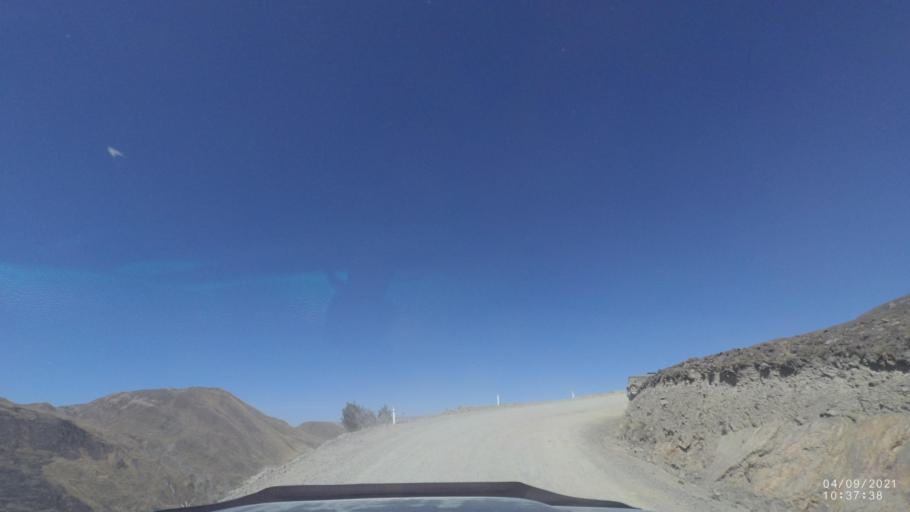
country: BO
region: Cochabamba
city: Sipe Sipe
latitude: -17.2884
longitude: -66.4561
